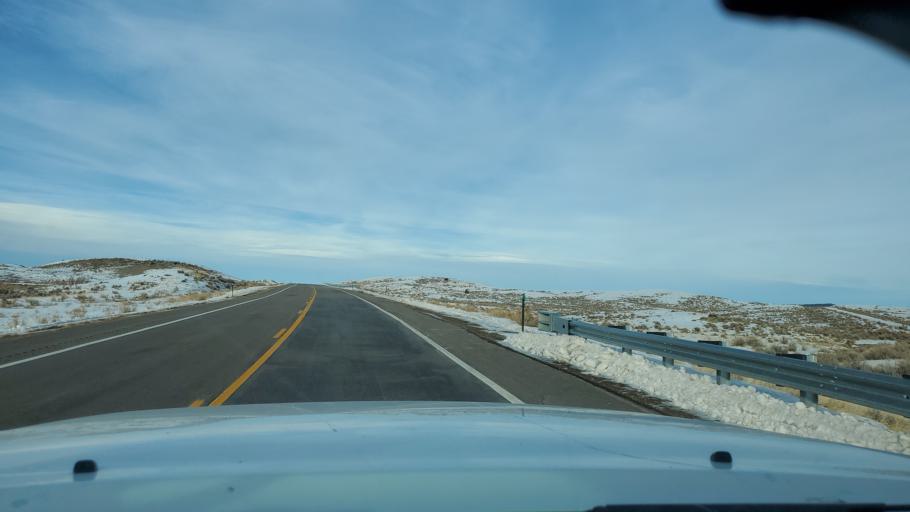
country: US
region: Colorado
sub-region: Rio Blanco County
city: Rangely
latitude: 40.3053
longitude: -108.5244
